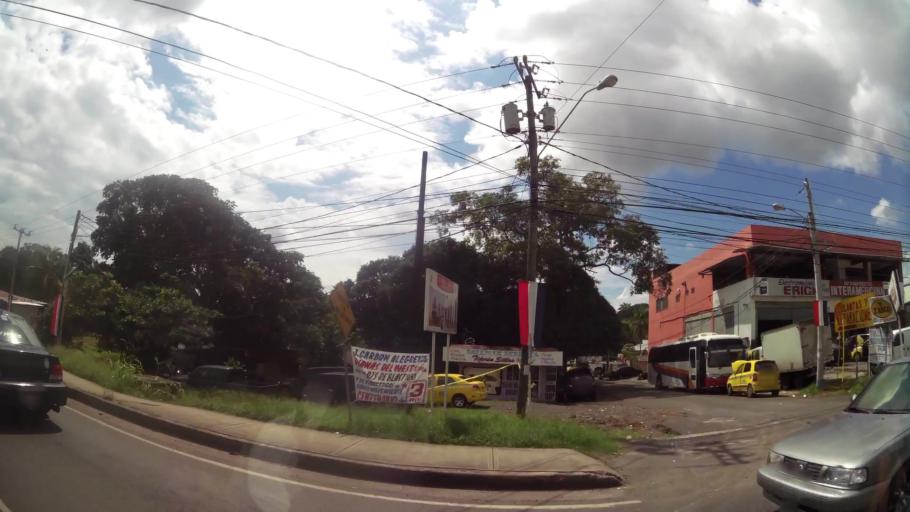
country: PA
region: Panama
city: Nuevo Arraijan
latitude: 8.9258
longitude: -79.7149
